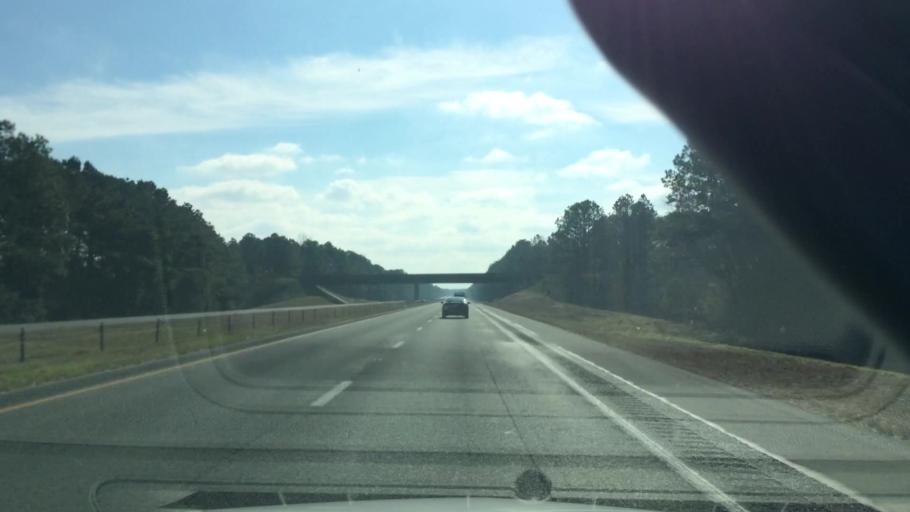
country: US
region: North Carolina
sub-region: Duplin County
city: Wallace
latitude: 34.7340
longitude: -77.9448
